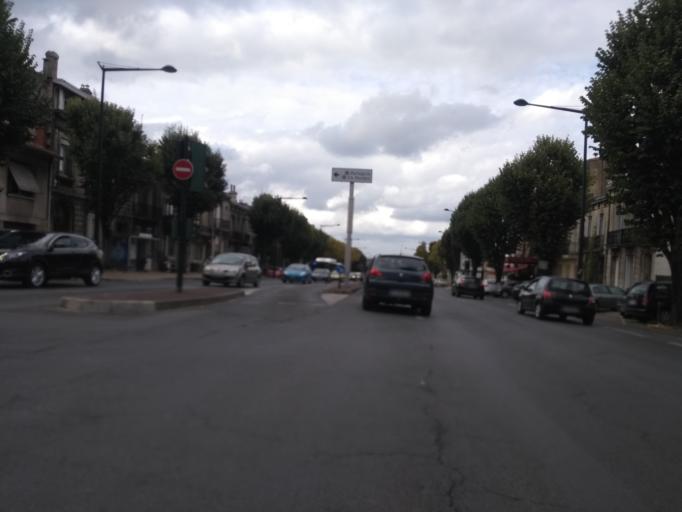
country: FR
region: Aquitaine
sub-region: Departement de la Gironde
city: Bordeaux
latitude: 44.8275
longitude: -0.5926
